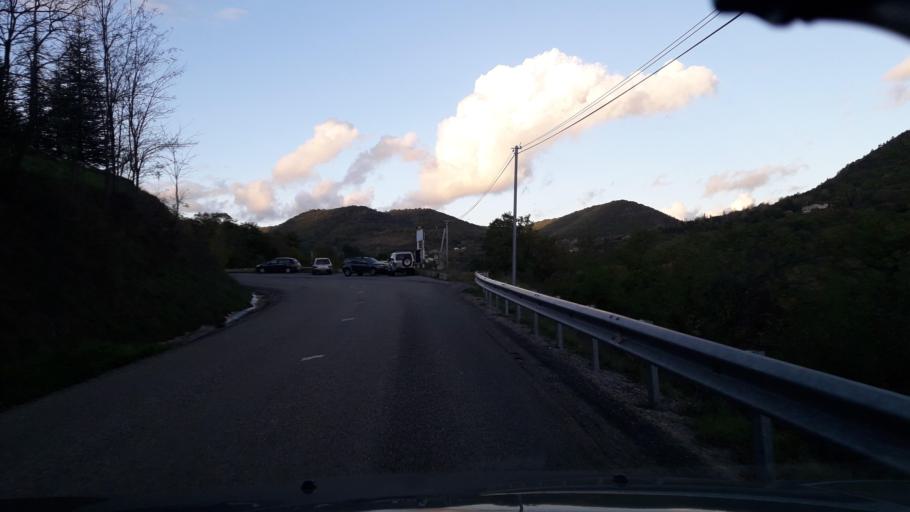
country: FR
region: Rhone-Alpes
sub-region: Departement de l'Ardeche
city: Vesseaux
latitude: 44.6353
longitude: 4.4973
